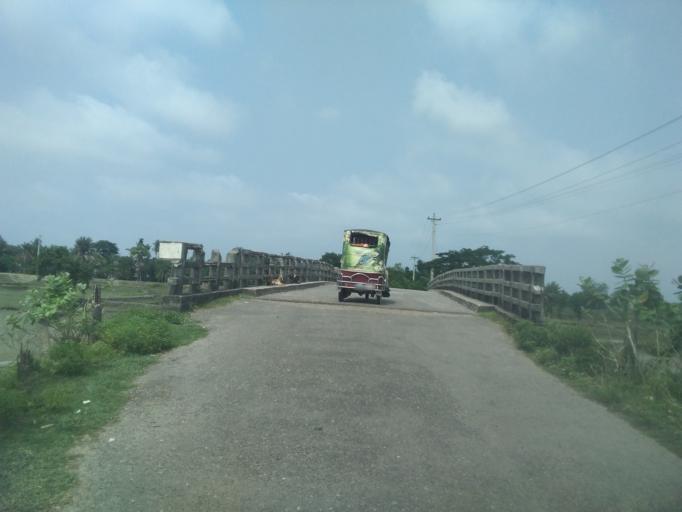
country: BD
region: Khulna
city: Phultala
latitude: 22.7045
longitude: 89.4682
